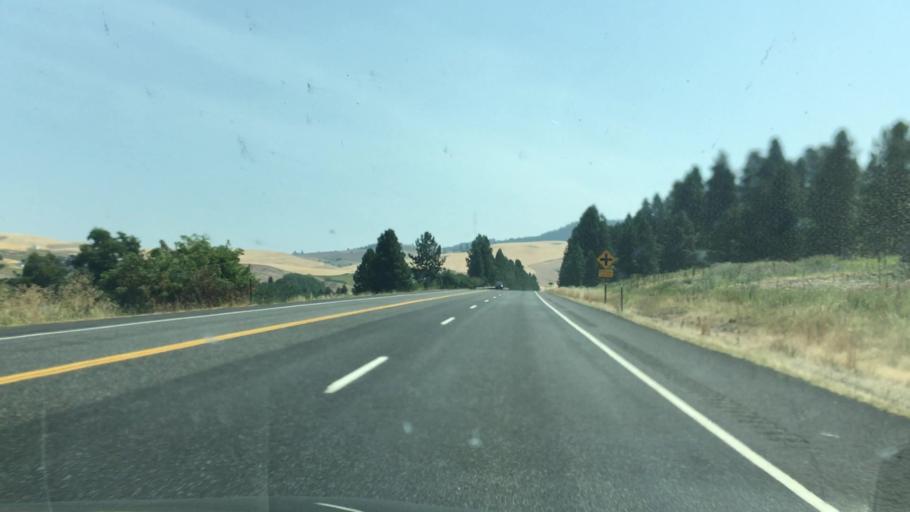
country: US
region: Idaho
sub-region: Nez Perce County
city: Lapwai
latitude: 46.3730
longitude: -116.6788
